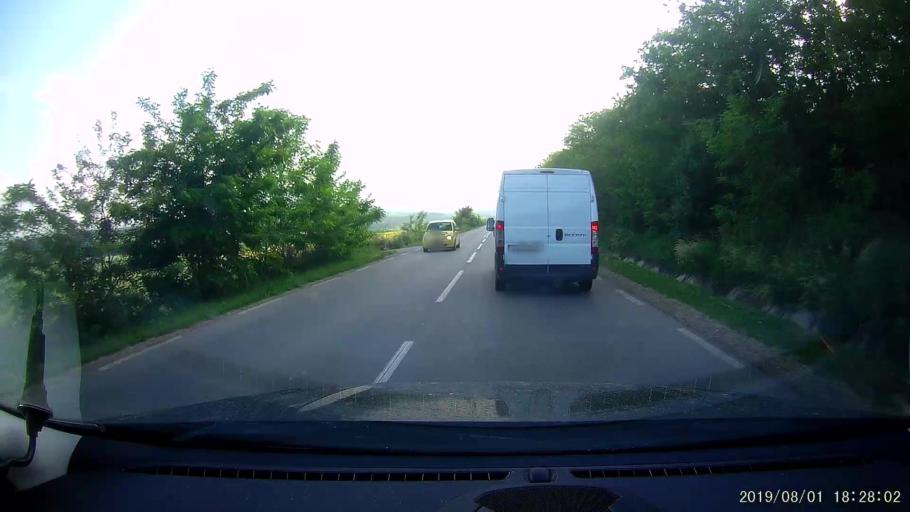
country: BG
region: Shumen
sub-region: Obshtina Venets
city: Venets
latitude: 43.5794
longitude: 26.9721
